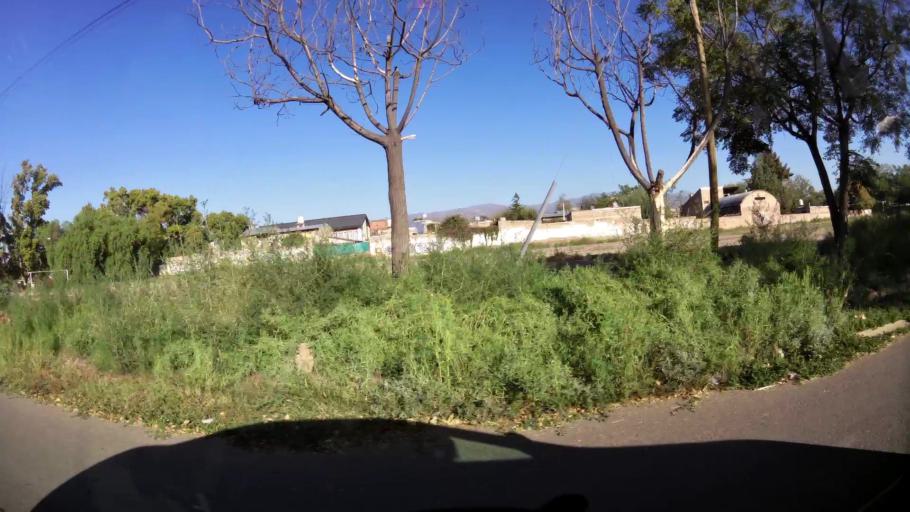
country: AR
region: Mendoza
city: Las Heras
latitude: -32.8581
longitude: -68.8195
